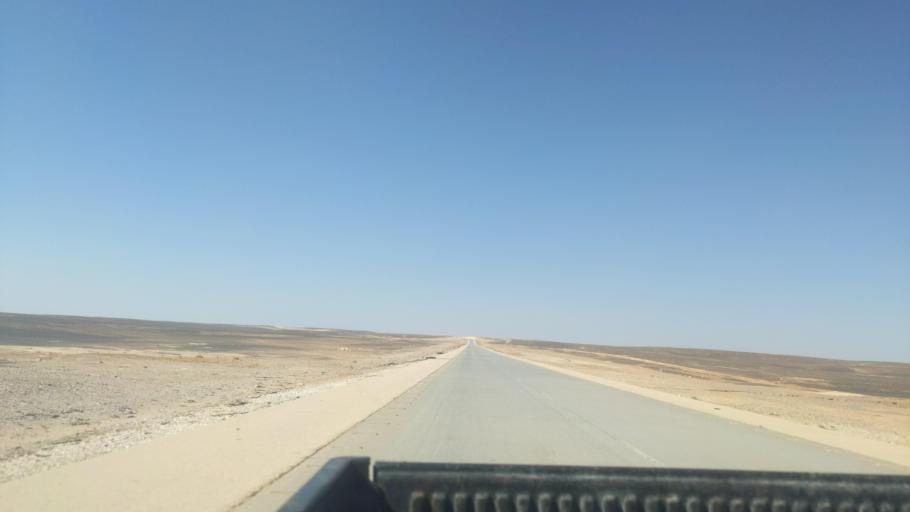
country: JO
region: Amman
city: Al Azraq ash Shamali
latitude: 31.4077
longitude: 36.7161
